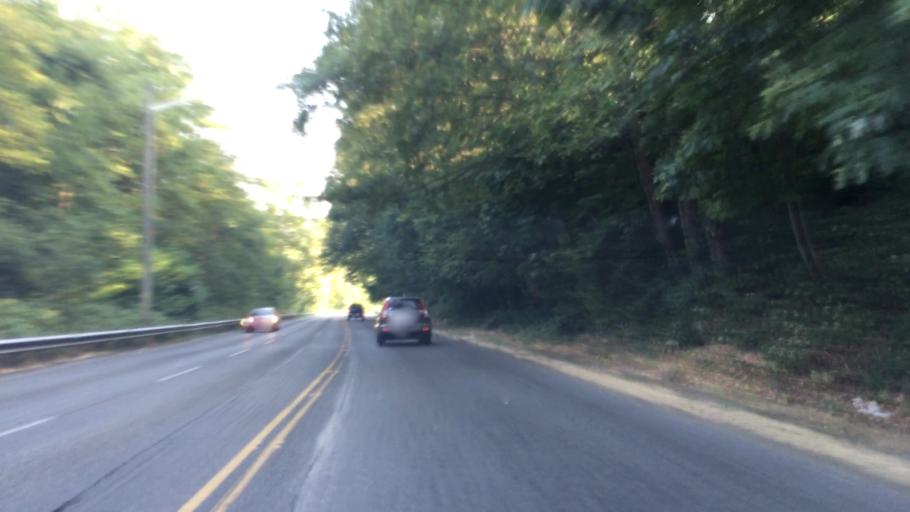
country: US
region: Washington
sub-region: Pierce County
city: Fife Heights
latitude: 47.2805
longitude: -122.3673
